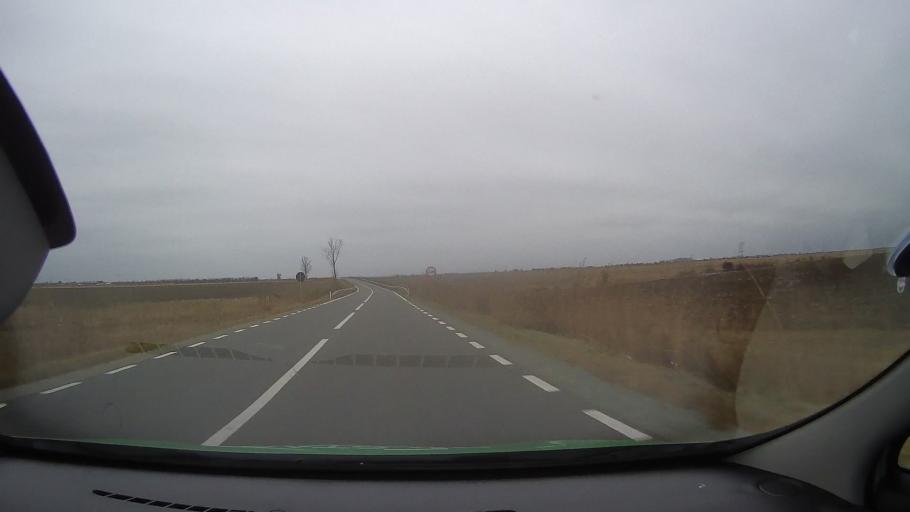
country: RO
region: Ialomita
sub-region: Comuna Slobozia
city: Slobozia
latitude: 44.6199
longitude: 27.3893
